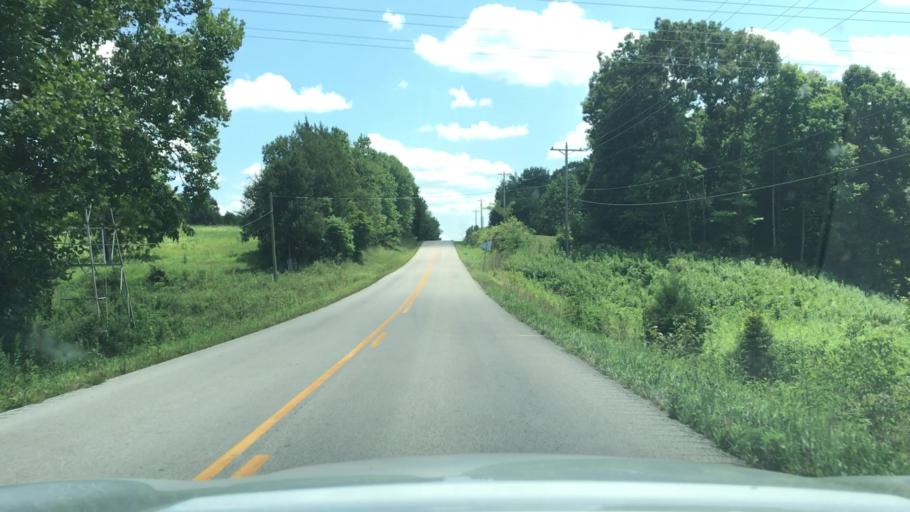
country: US
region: Kentucky
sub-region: Christian County
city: Hopkinsville
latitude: 36.9964
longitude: -87.3648
